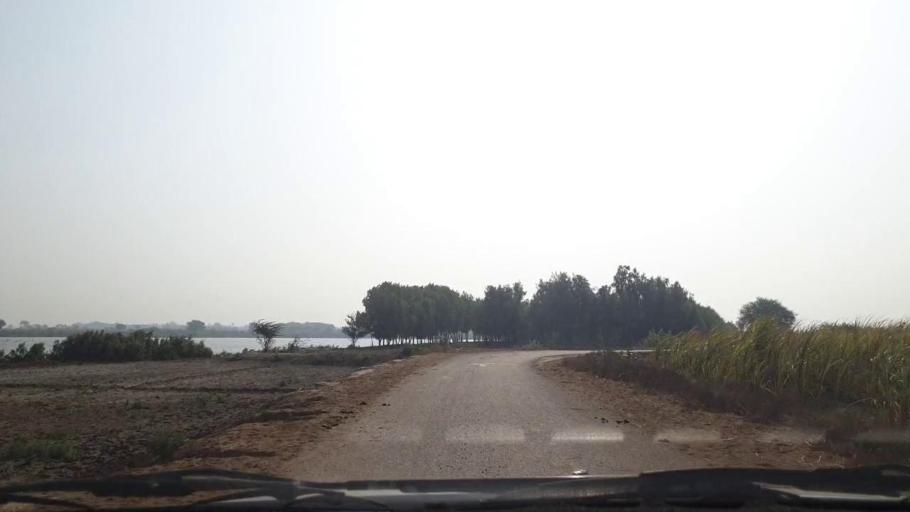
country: PK
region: Sindh
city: Tando Muhammad Khan
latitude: 25.0053
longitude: 68.4518
